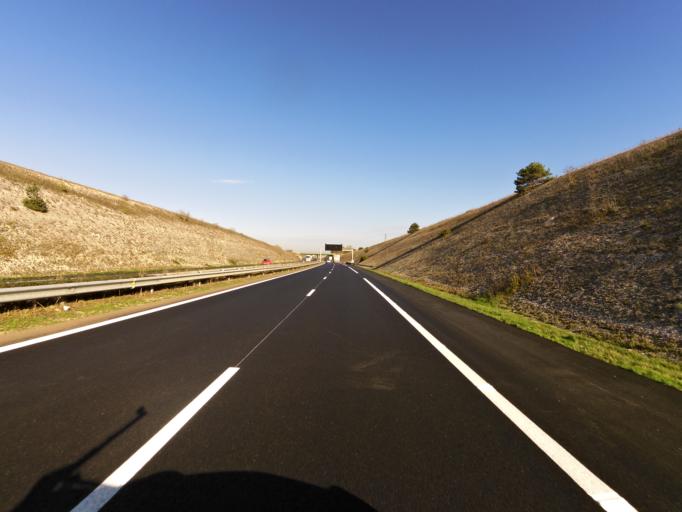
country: FR
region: Champagne-Ardenne
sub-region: Departement de la Marne
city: Fagnieres
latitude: 48.9450
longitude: 4.2892
